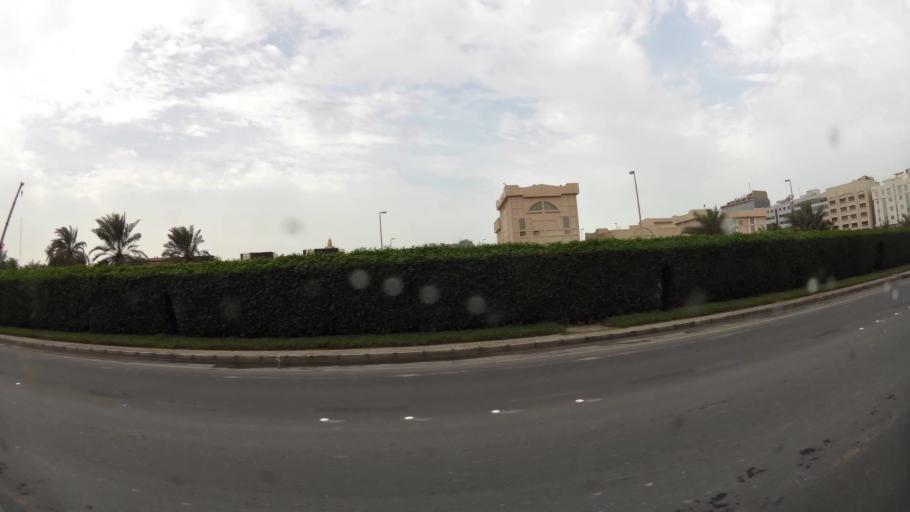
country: AE
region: Abu Dhabi
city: Abu Dhabi
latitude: 24.4785
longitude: 54.3878
